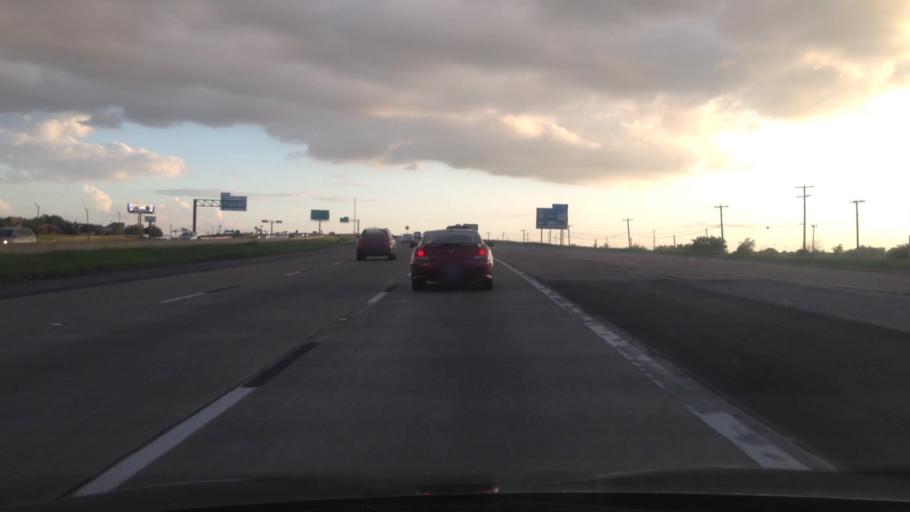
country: US
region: Texas
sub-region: Tarrant County
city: White Settlement
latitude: 32.7787
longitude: -97.4726
